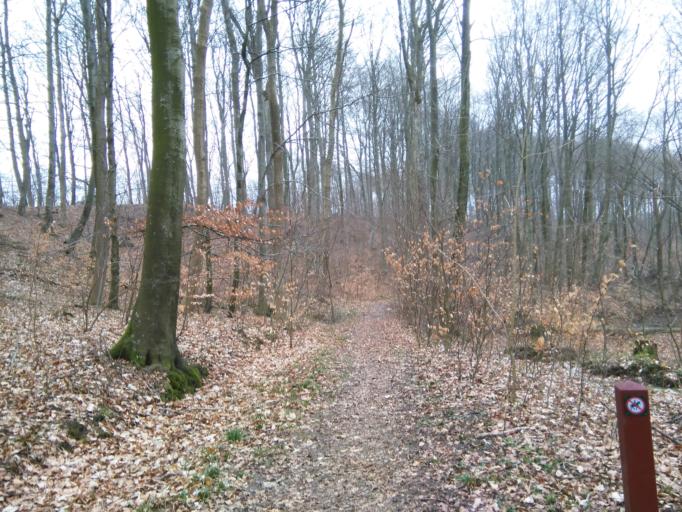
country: DK
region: Central Jutland
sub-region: Arhus Kommune
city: Beder
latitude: 56.0682
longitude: 10.1993
